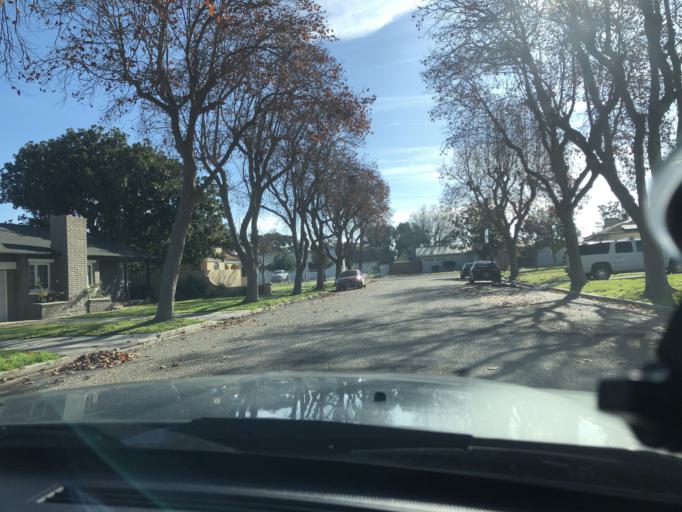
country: US
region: California
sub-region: Monterey County
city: King City
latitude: 36.2070
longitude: -121.1311
